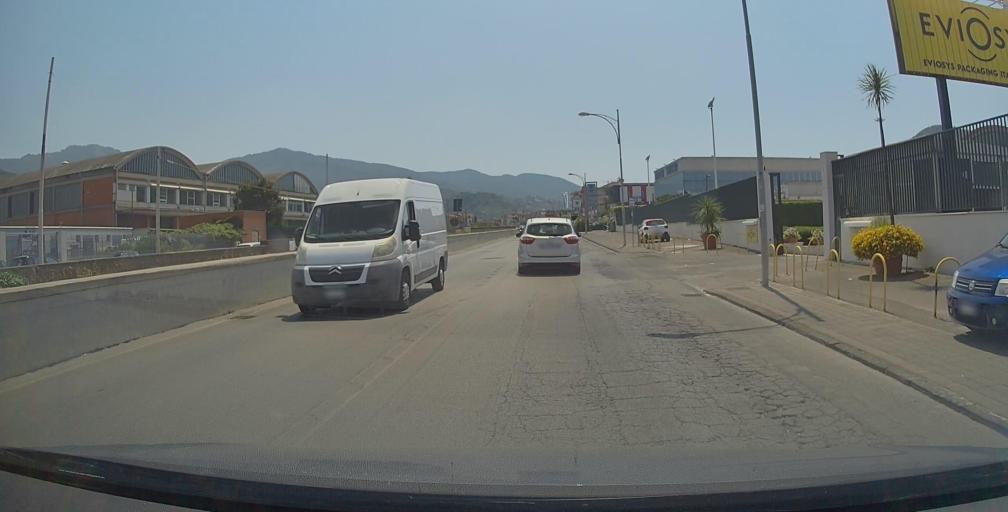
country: IT
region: Campania
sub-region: Provincia di Salerno
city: Nocera Superiore
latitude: 40.7362
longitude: 14.6791
